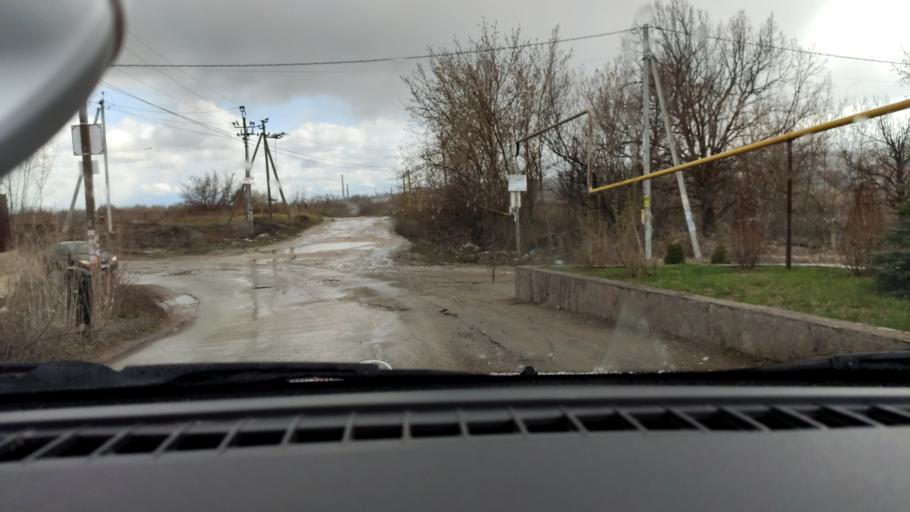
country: RU
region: Samara
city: Novosemeykino
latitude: 53.3261
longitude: 50.2908
